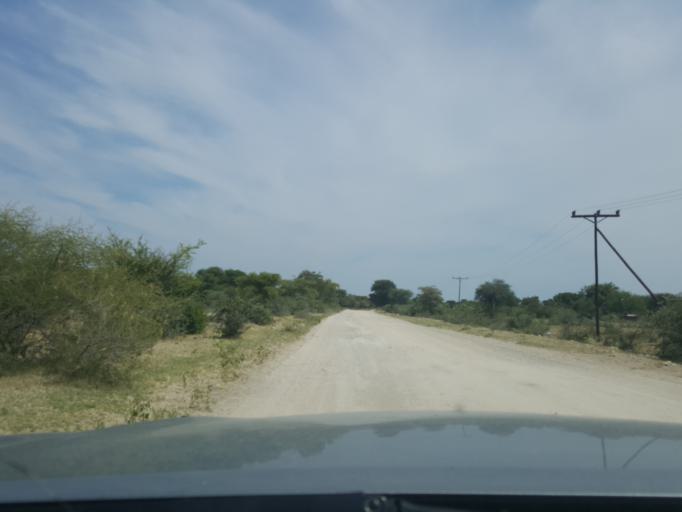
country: BW
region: North West
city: Shakawe
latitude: -18.3166
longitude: 21.9042
